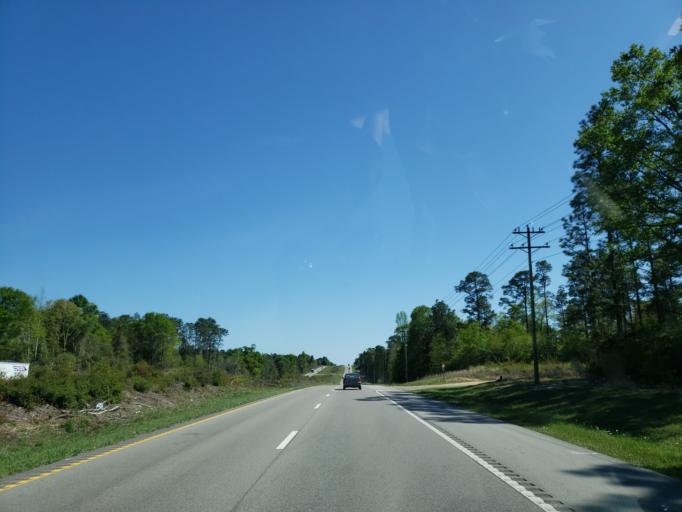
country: US
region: Mississippi
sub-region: Stone County
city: Wiggins
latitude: 30.9295
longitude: -89.1792
